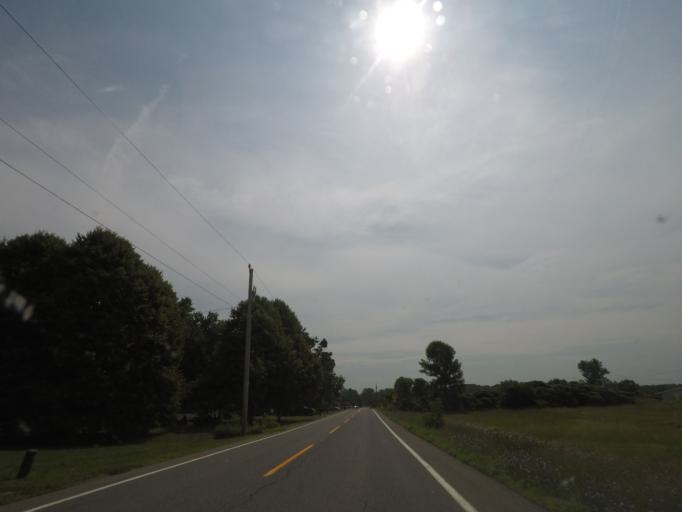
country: US
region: New York
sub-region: Saratoga County
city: Mechanicville
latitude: 42.8867
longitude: -73.7049
